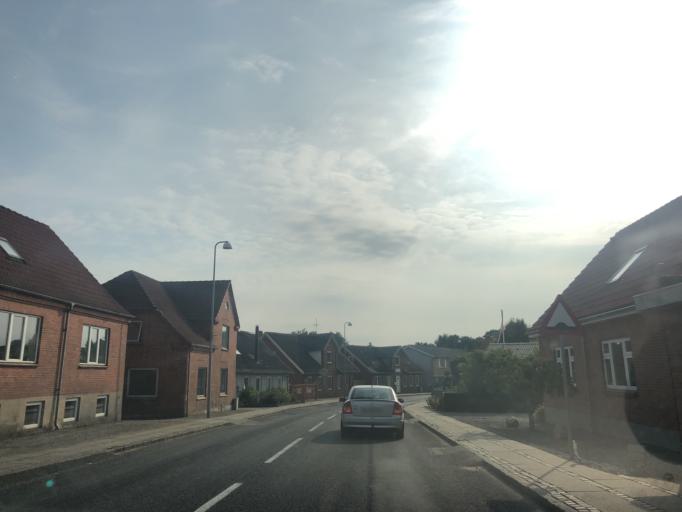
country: DK
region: Central Jutland
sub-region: Skive Kommune
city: Skive
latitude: 56.7017
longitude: 8.9942
